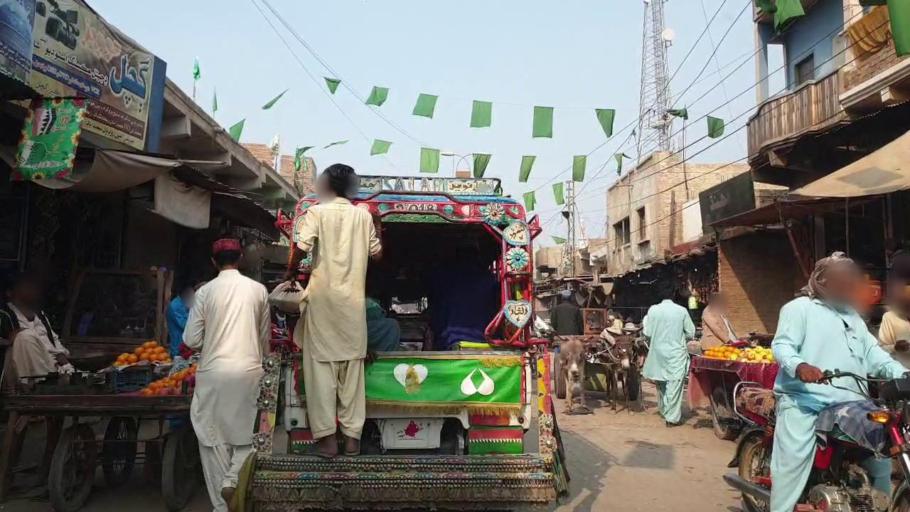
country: PK
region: Sindh
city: Bhan
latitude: 26.5568
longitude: 67.7207
